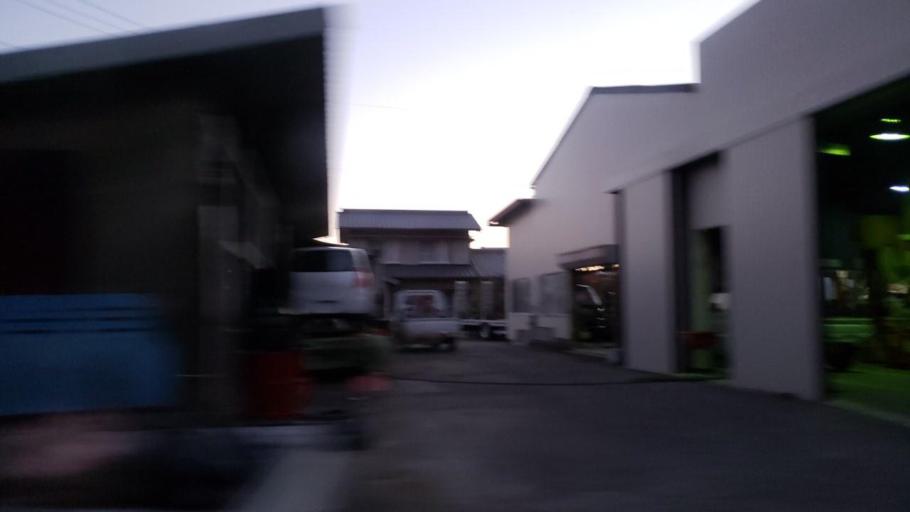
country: JP
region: Tokushima
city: Kamojimacho-jogejima
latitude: 34.1010
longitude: 134.3126
